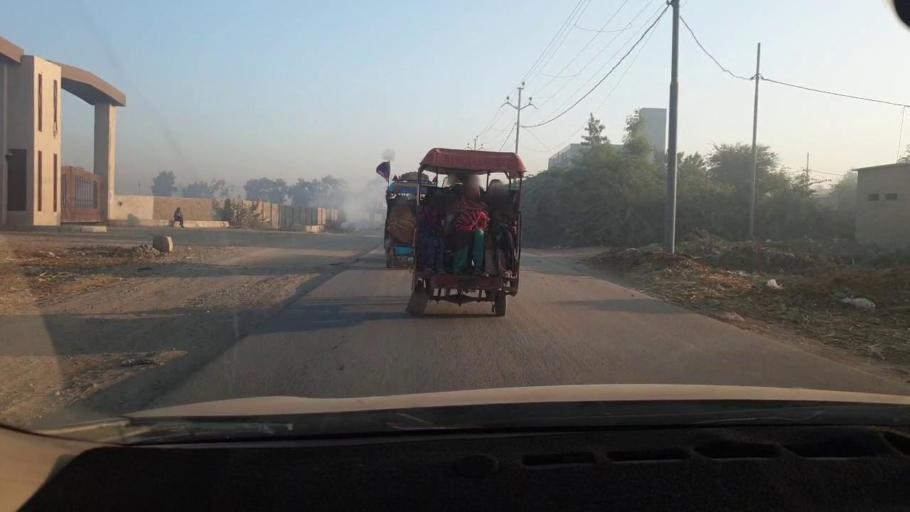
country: PK
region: Sindh
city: Malir Cantonment
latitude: 25.0043
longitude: 67.1526
